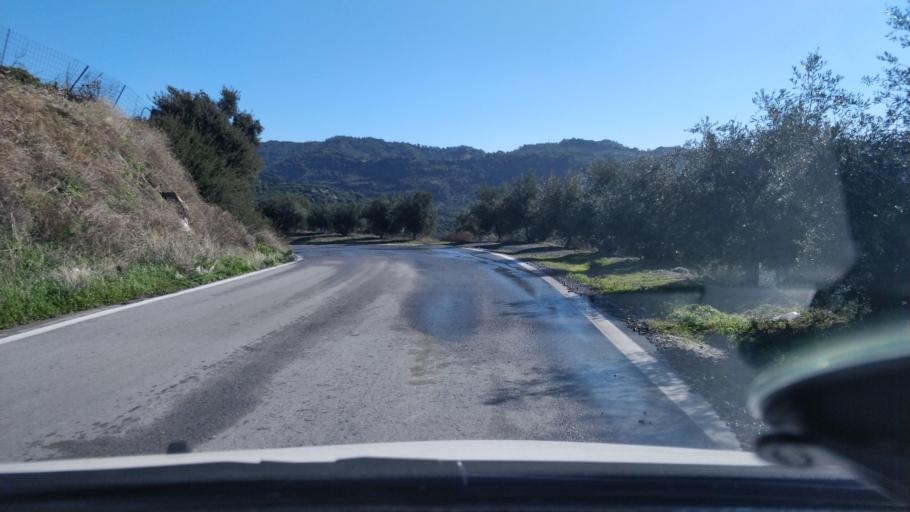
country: GR
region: Crete
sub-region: Nomos Irakleiou
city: Kastelli
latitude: 35.0333
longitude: 25.4470
